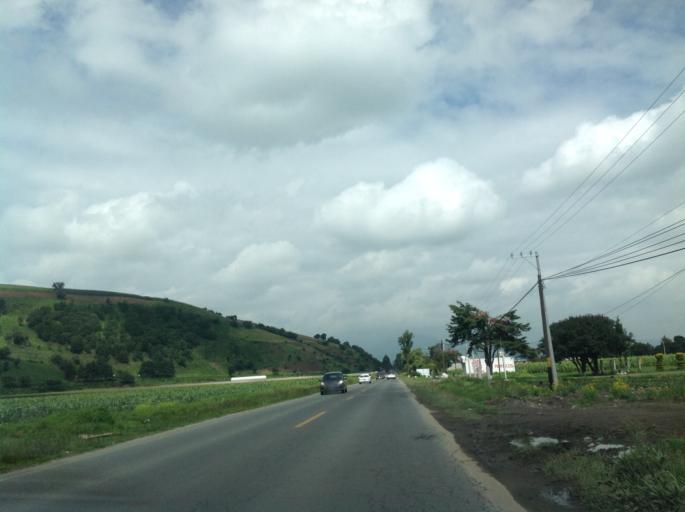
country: MX
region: Mexico
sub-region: Tenango del Valle
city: Santa Maria Jajalpa
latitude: 19.1166
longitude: -99.5444
